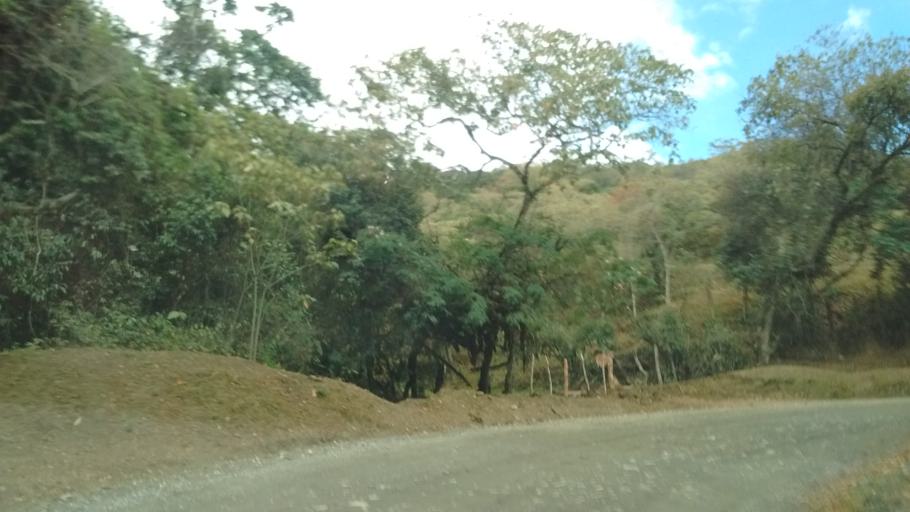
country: CO
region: Cauca
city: Almaguer
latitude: 1.8573
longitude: -76.9312
